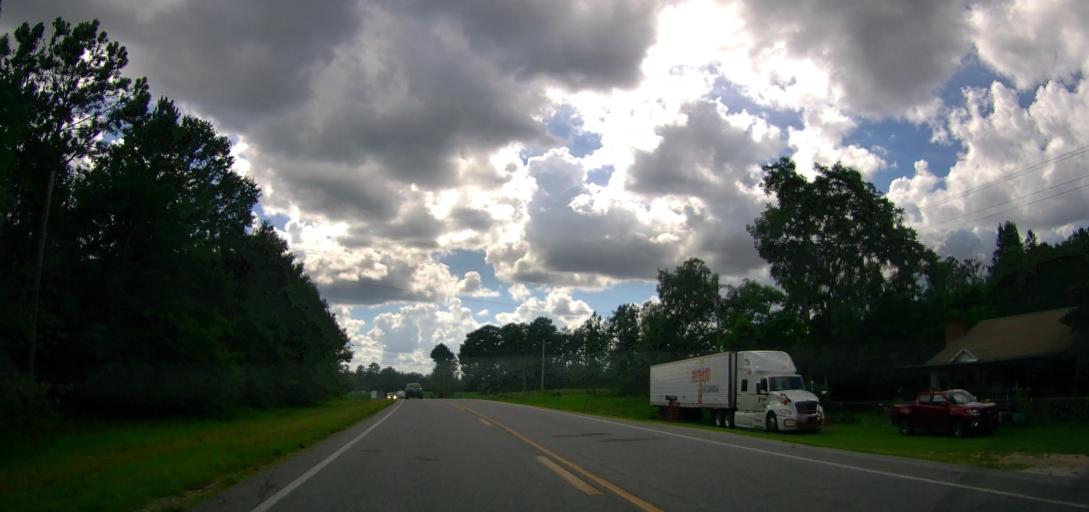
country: US
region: Alabama
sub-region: Russell County
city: Ladonia
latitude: 32.4507
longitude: -85.2301
